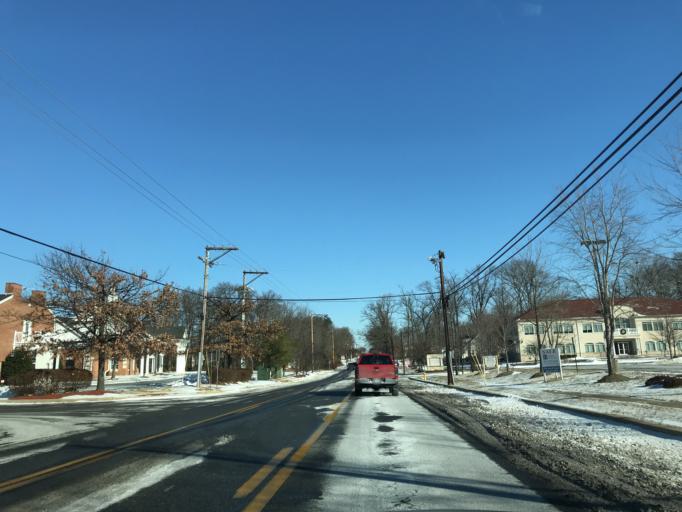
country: US
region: Maryland
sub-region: Charles County
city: Waldorf
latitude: 38.6170
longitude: -76.9161
